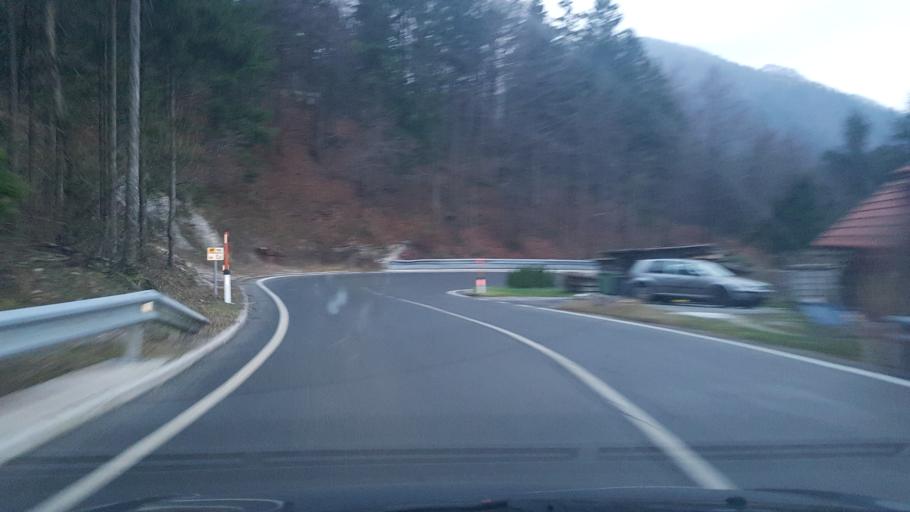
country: SI
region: Idrija
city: Idrija
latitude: 45.9220
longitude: 14.0454
